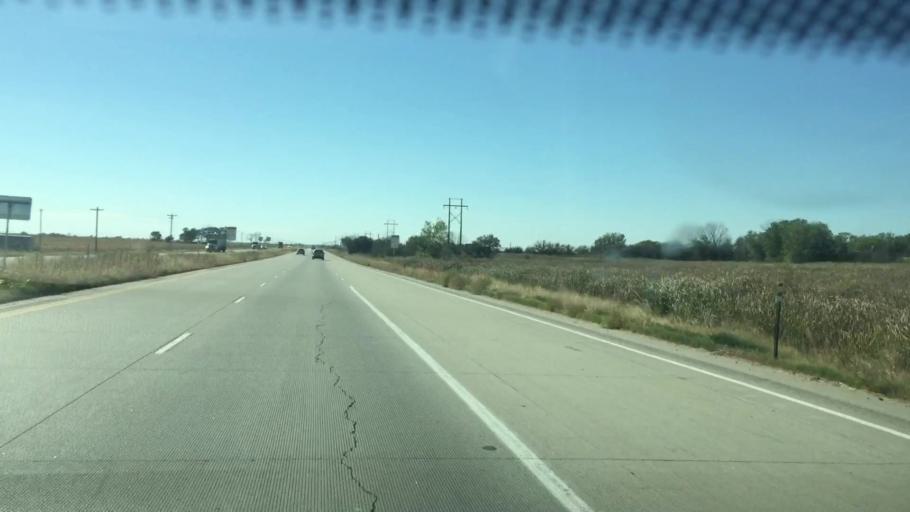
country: US
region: Colorado
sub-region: Prowers County
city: Lamar
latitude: 38.1120
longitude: -102.6530
